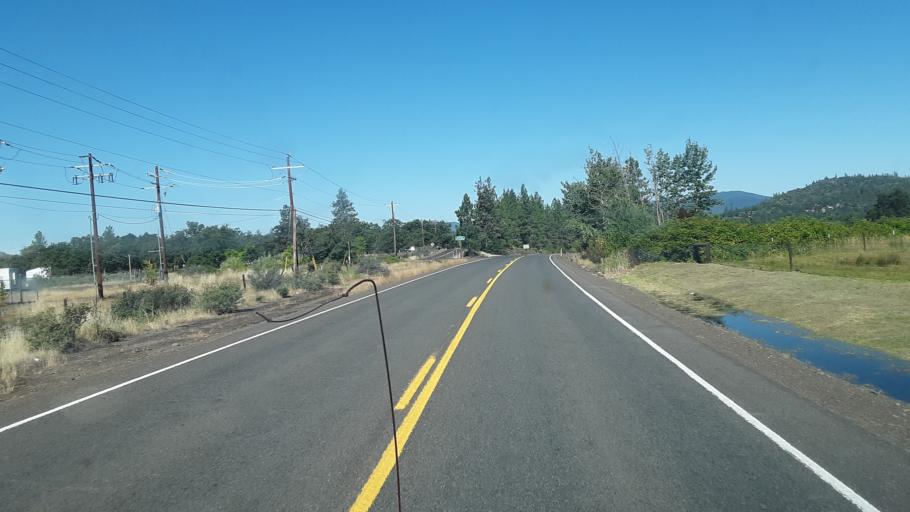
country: US
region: Oregon
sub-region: Jackson County
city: Eagle Point
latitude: 42.5237
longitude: -122.8327
